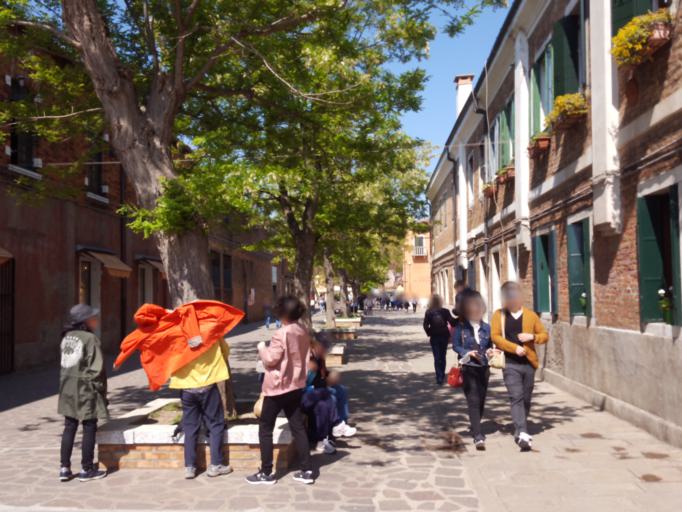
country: IT
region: Veneto
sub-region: Provincia di Venezia
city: Murano
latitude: 45.4529
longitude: 12.3542
